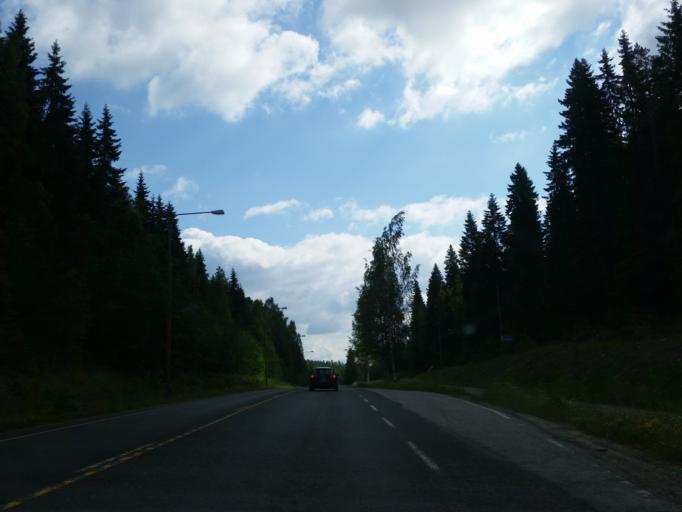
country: FI
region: Northern Savo
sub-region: Kuopio
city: Kuopio
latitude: 62.8388
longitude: 27.5723
